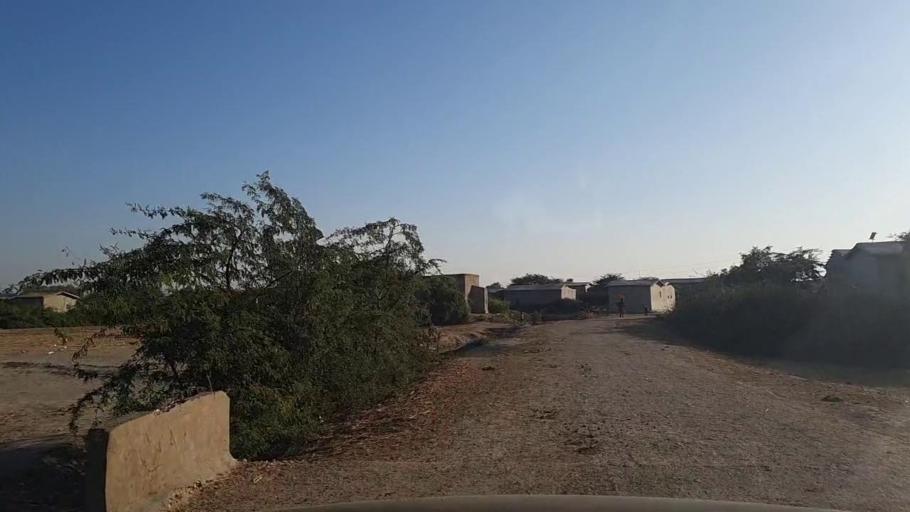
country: PK
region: Sindh
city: Mirpur Batoro
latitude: 24.7041
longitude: 68.3087
